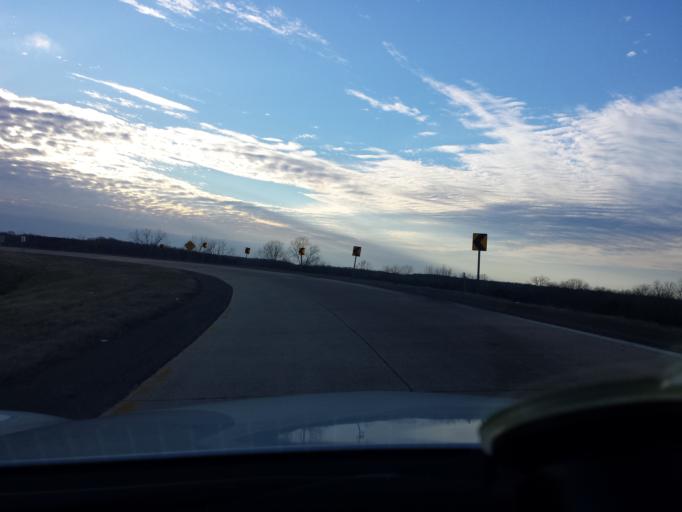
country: US
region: Mississippi
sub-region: Oktibbeha County
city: Starkville
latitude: 33.4973
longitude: -88.8483
